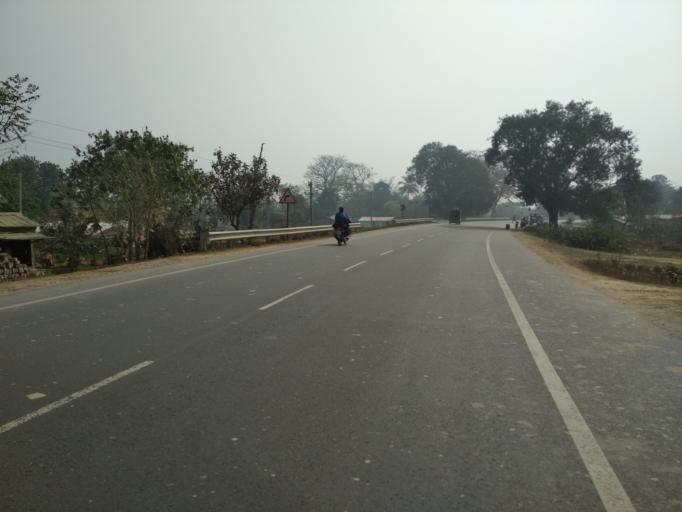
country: IN
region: Bihar
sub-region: Khagaria
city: Khagaria
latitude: 25.4997
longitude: 86.5937
